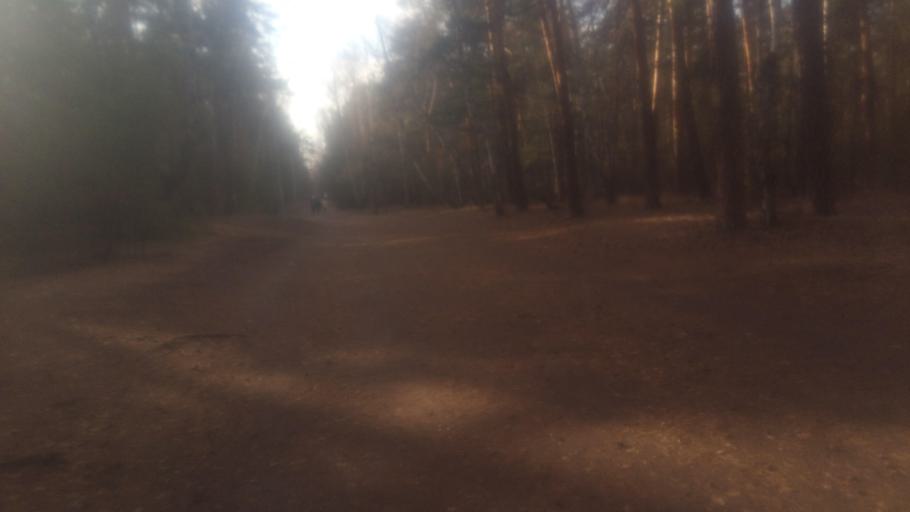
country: RU
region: Chelyabinsk
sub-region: Gorod Chelyabinsk
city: Chelyabinsk
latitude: 55.1646
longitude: 61.3581
